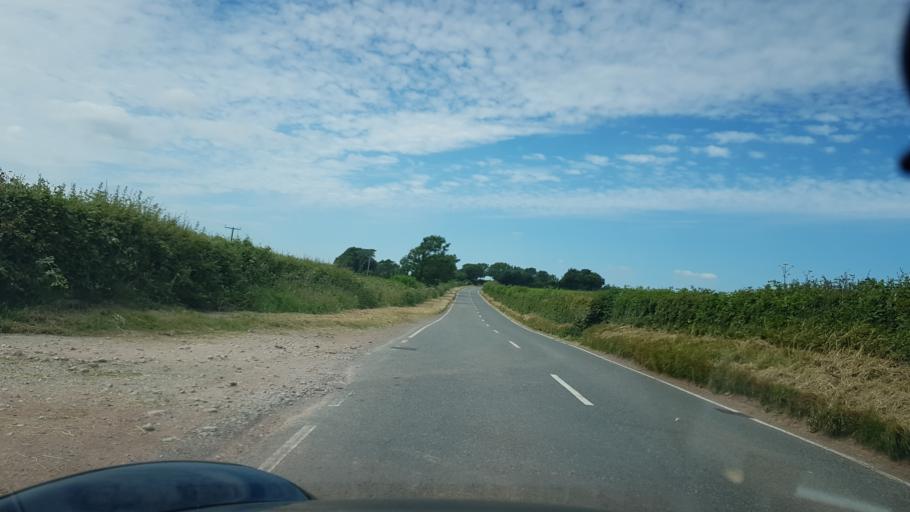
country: GB
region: Wales
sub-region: Carmarthenshire
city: Whitland
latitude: 51.7685
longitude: -4.5888
